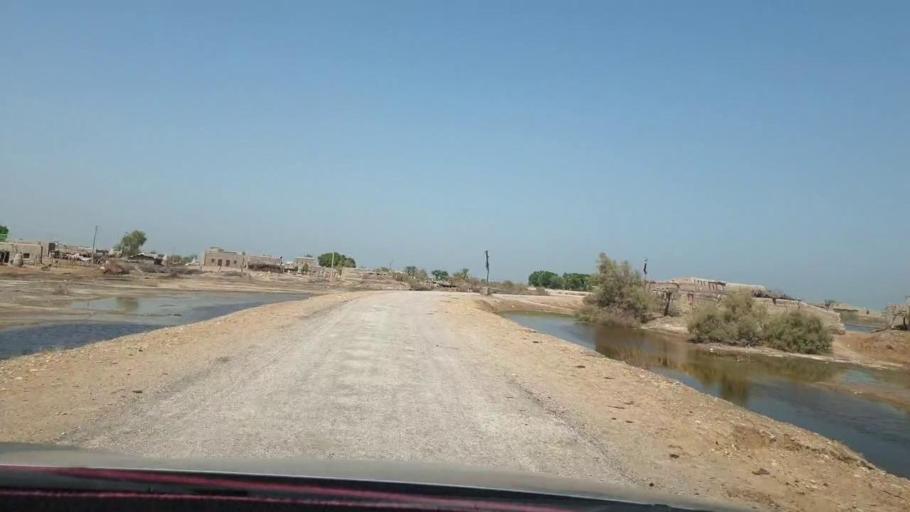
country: PK
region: Sindh
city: Warah
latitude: 27.5759
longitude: 67.7571
